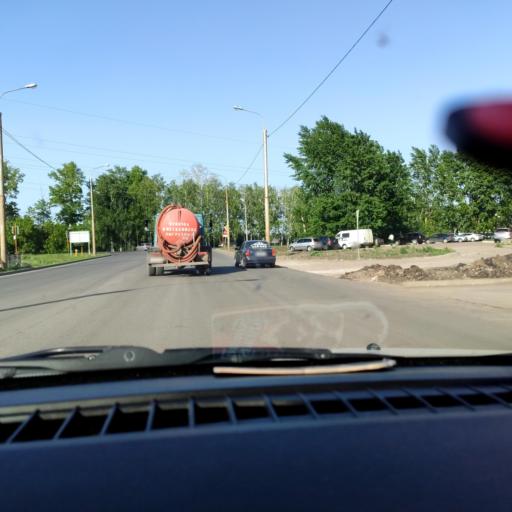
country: RU
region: Bashkortostan
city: Sterlitamak
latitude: 53.6407
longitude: 55.8982
